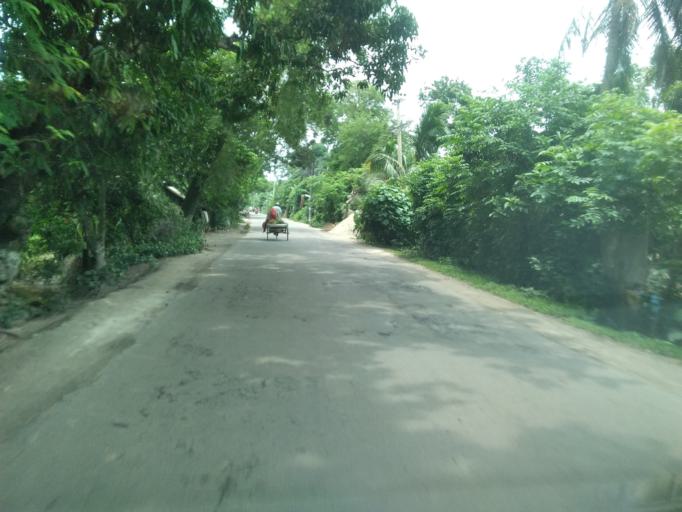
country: IN
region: West Bengal
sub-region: North 24 Parganas
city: Taki
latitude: 22.5590
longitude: 89.0051
